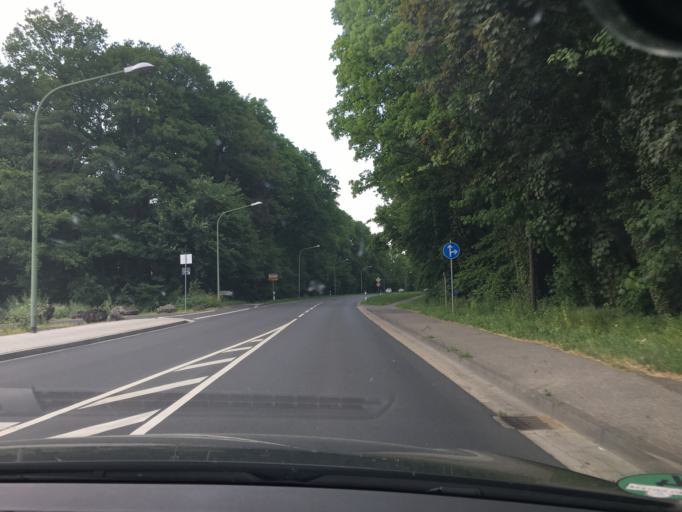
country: DE
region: North Rhine-Westphalia
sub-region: Regierungsbezirk Koln
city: Dueren
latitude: 50.7797
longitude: 6.4888
